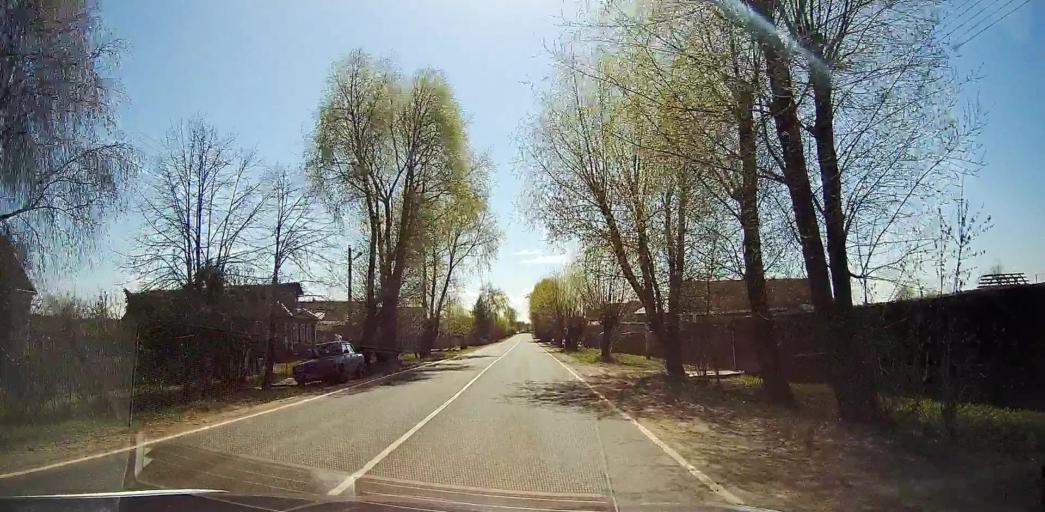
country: RU
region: Moskovskaya
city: Beloozerskiy
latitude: 55.5143
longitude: 38.4323
